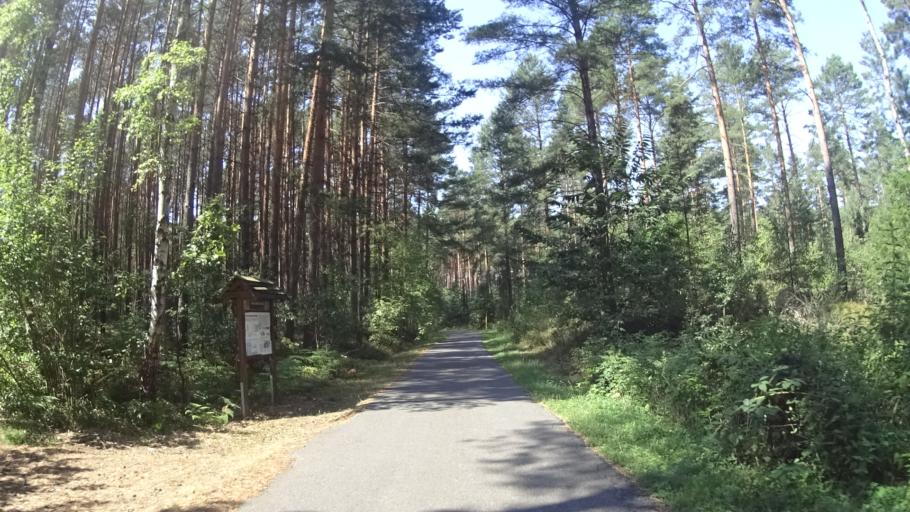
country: DE
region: Saxony
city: Gross Duben
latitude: 51.6099
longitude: 14.5509
